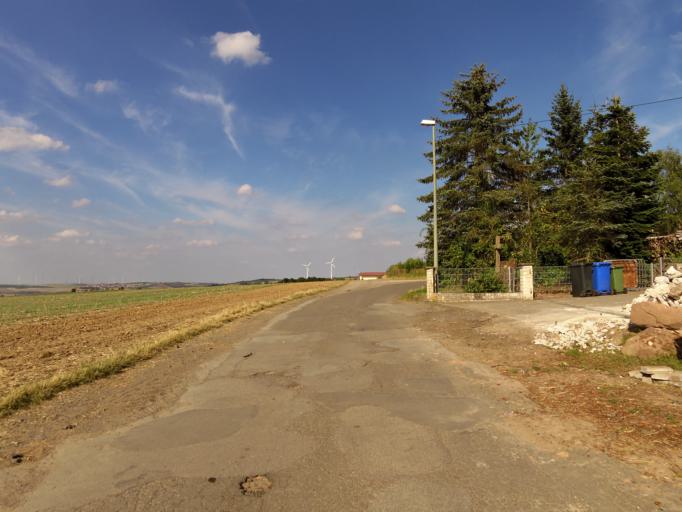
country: DE
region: Rheinland-Pfalz
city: Tiefenthal
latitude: 49.5274
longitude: 8.0942
